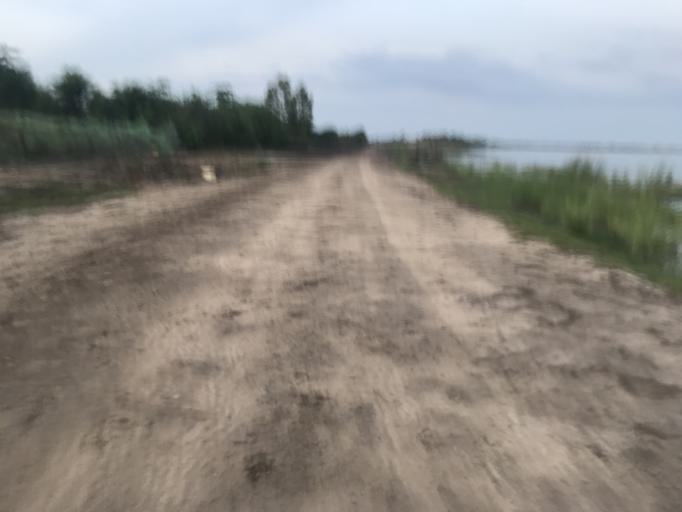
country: SN
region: Saint-Louis
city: Saint-Louis
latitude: 16.0502
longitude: -16.4130
